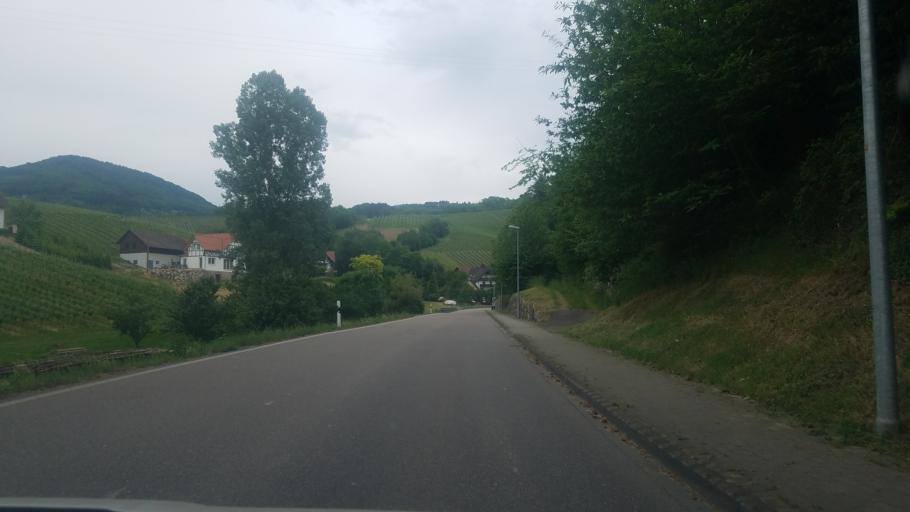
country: DE
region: Baden-Wuerttemberg
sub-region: Freiburg Region
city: Sasbachwalden
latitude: 48.6196
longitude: 8.1127
